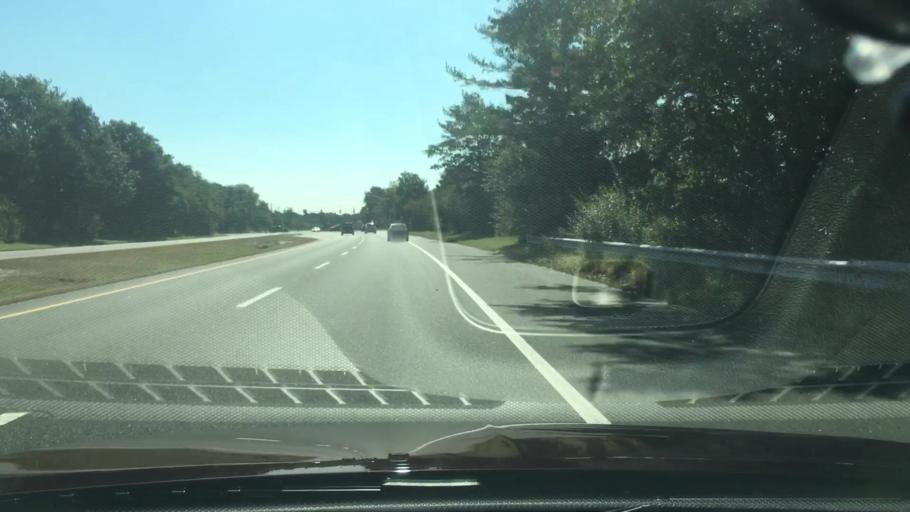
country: US
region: New York
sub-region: Suffolk County
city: North Bellport
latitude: 40.7994
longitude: -72.9596
